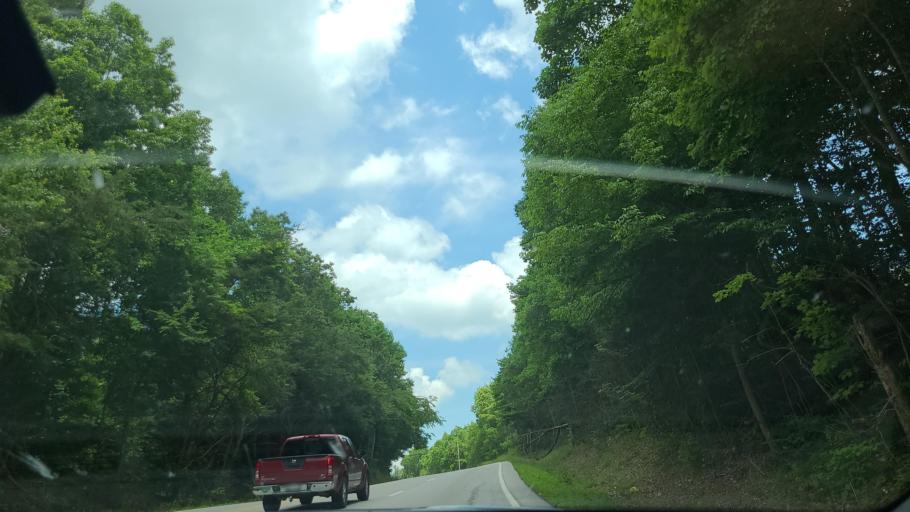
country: US
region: Tennessee
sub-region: Cumberland County
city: Lake Tansi
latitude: 35.7759
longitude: -85.0386
